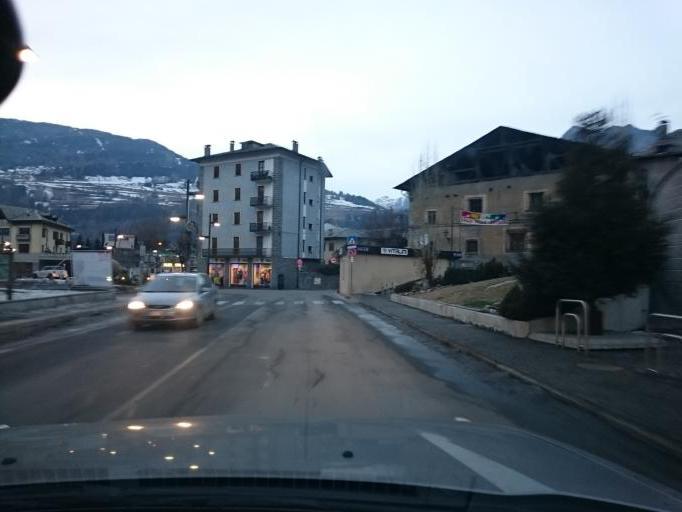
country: IT
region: Lombardy
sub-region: Provincia di Sondrio
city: Bormio
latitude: 46.4665
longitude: 10.3720
